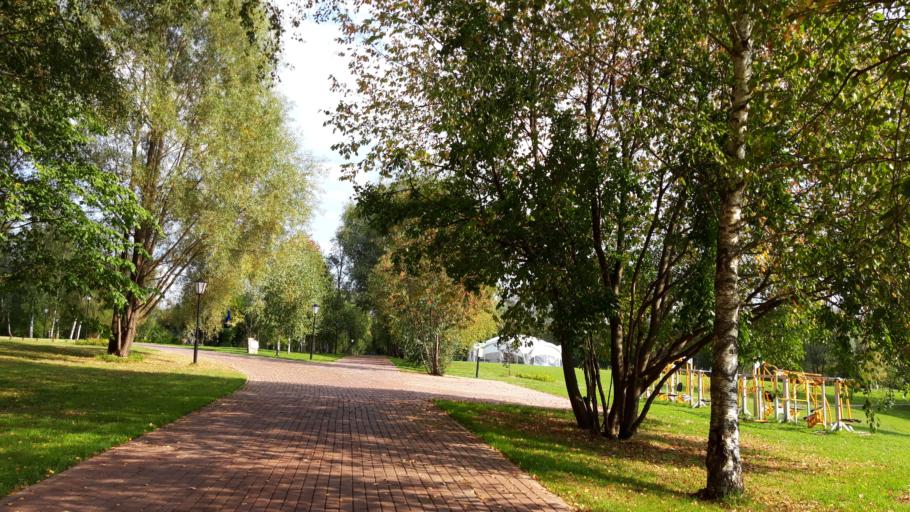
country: RU
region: Moskovskaya
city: Mendeleyevo
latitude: 56.0479
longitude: 37.2190
